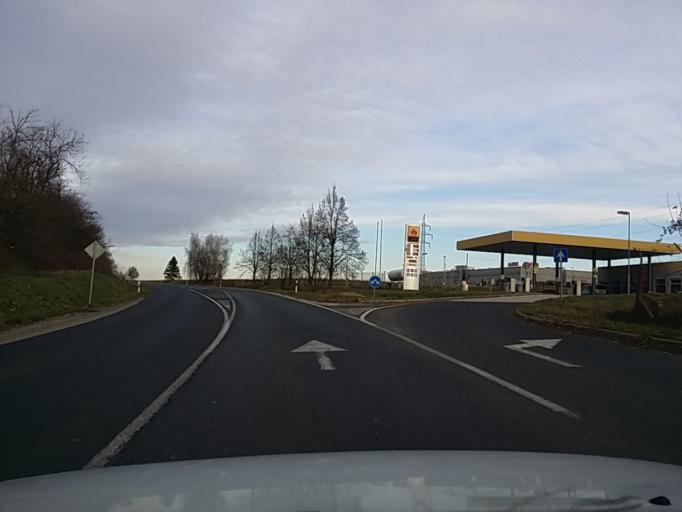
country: HU
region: Veszprem
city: Nemesvamos
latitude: 47.0647
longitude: 17.8723
